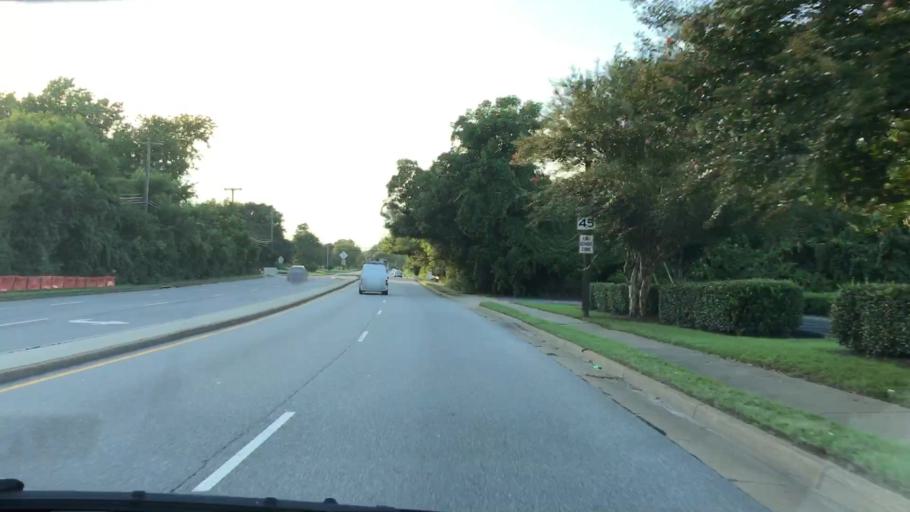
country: US
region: Virginia
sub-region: City of Hampton
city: Hampton
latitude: 37.0546
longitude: -76.3799
